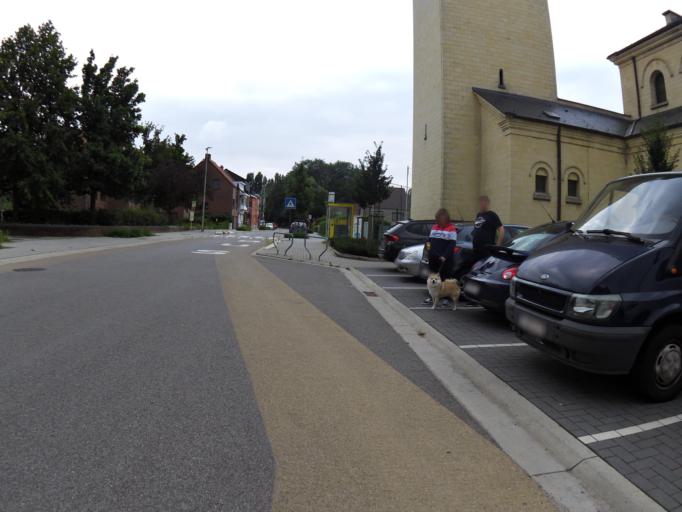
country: BE
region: Flanders
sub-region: Provincie Limburg
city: Tongeren
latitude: 50.7829
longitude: 5.4766
